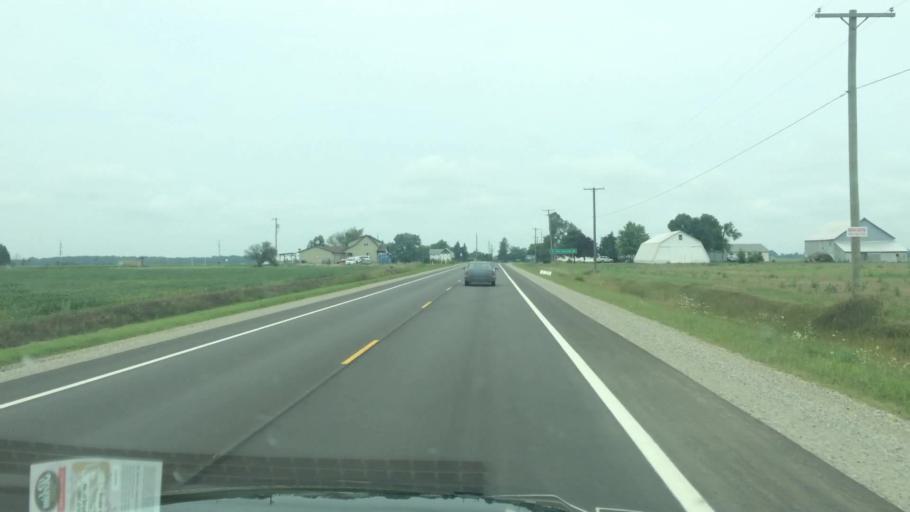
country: US
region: Michigan
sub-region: Huron County
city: Bad Axe
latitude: 44.0008
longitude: -83.0078
